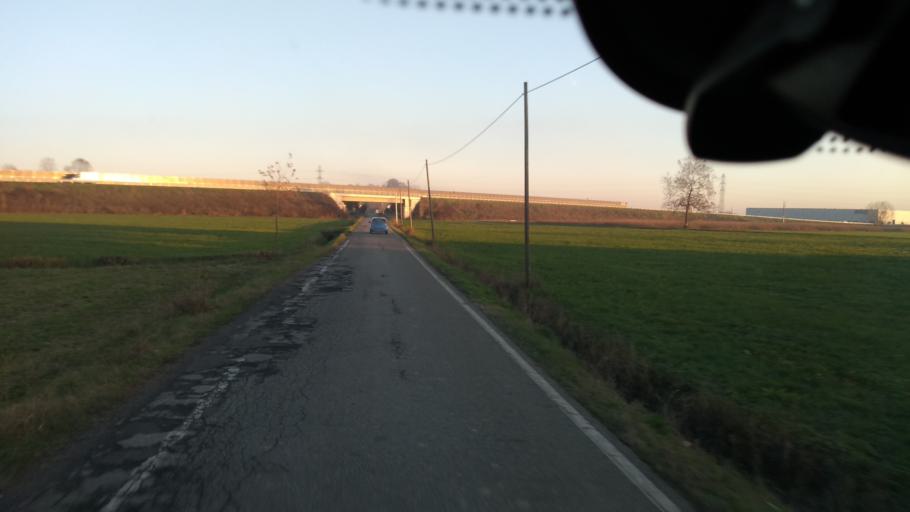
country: IT
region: Lombardy
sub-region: Provincia di Bergamo
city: Casirate d'Adda
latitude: 45.4971
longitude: 9.5553
